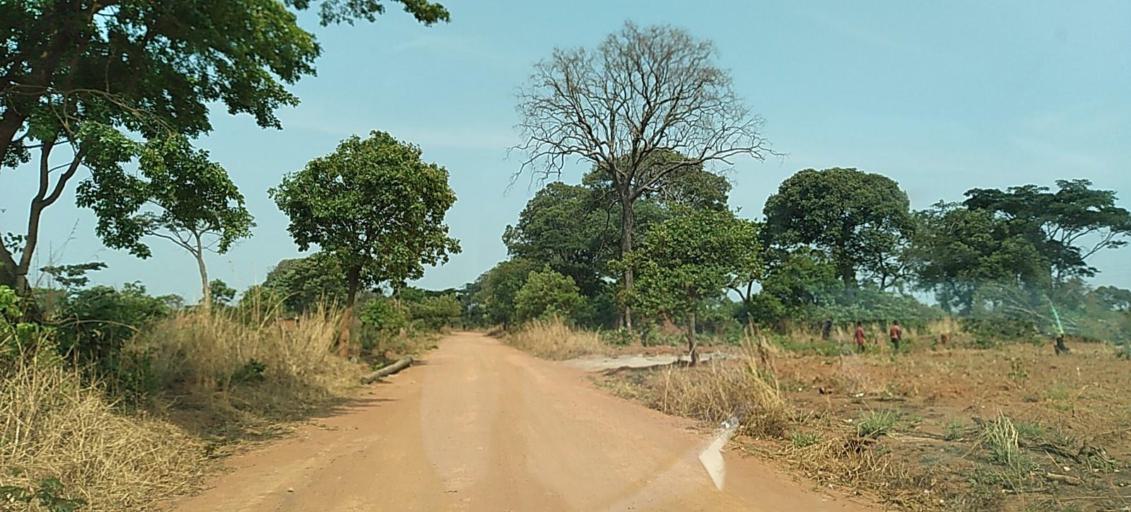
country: ZM
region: Copperbelt
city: Chililabombwe
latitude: -12.3408
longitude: 27.6949
